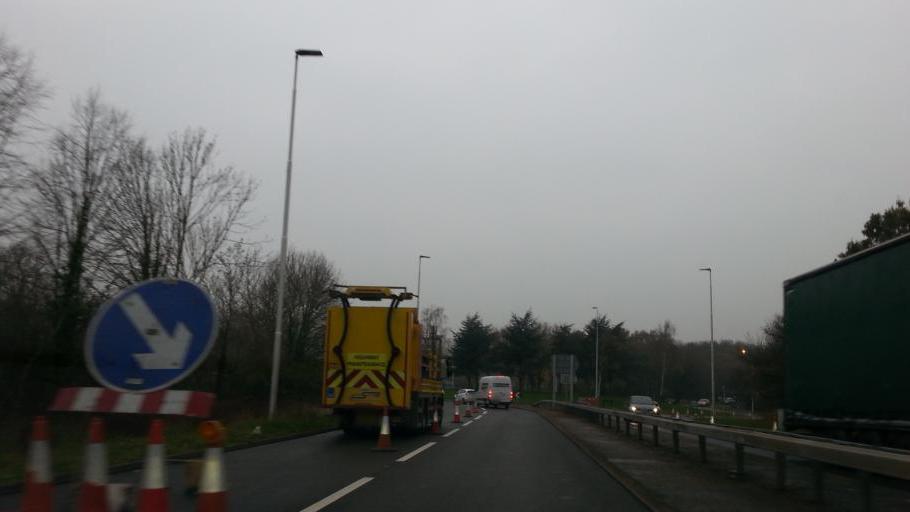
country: GB
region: England
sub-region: Peterborough
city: Castor
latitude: 52.5512
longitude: -0.3116
